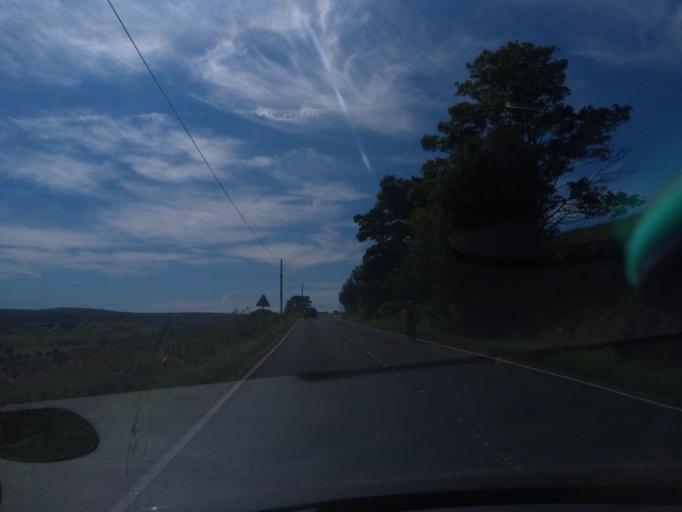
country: GB
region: England
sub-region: Northumberland
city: Bardon Mill
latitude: 54.8738
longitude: -2.3541
